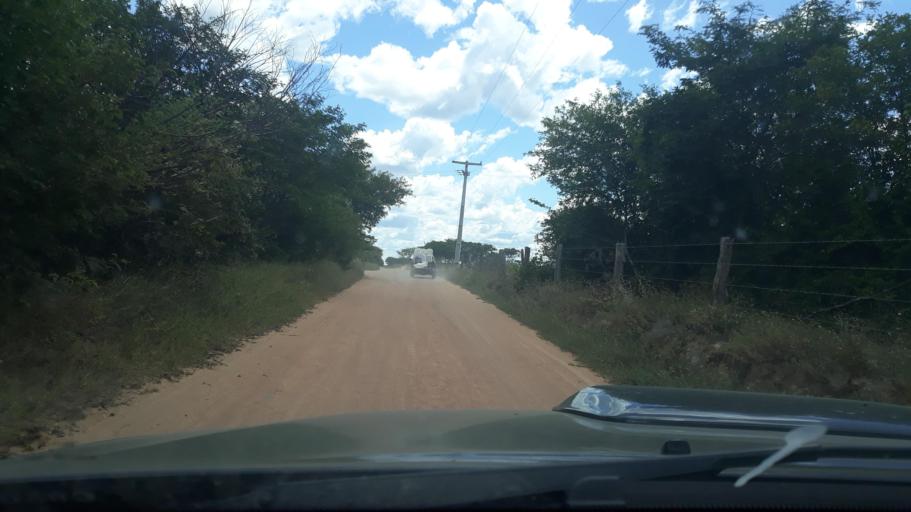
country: BR
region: Bahia
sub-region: Riacho De Santana
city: Riacho de Santana
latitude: -13.9059
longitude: -42.9276
